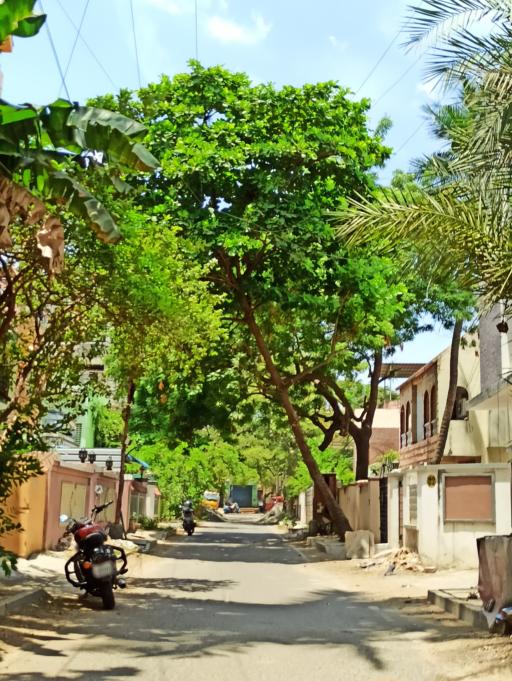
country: IN
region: Tamil Nadu
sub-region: Chennai
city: Chetput
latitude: 13.0607
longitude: 80.2224
